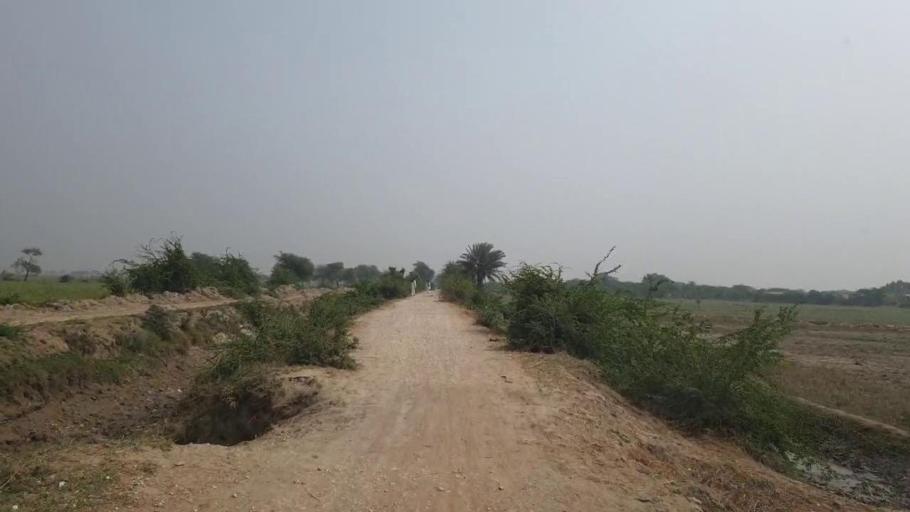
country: PK
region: Sindh
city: Kario
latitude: 24.6510
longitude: 68.6078
